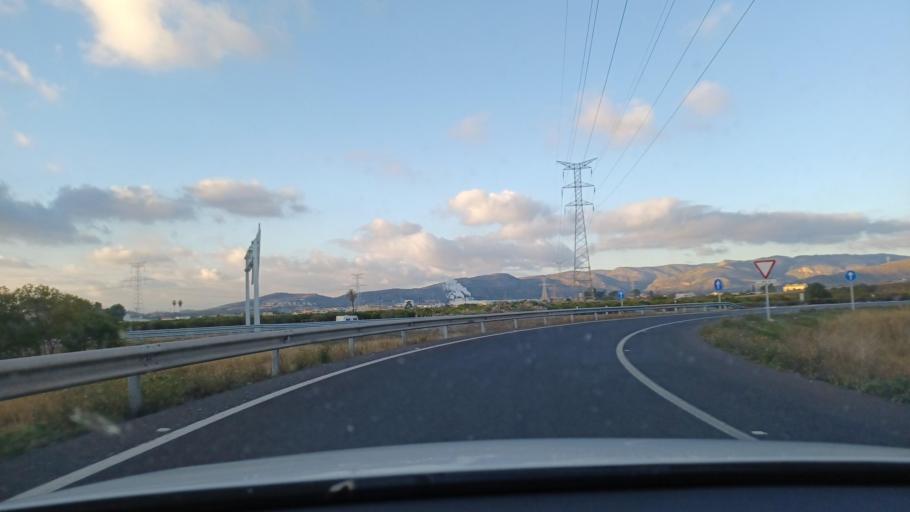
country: ES
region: Valencia
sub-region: Provincia de Castello
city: Vila-real
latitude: 39.9841
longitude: -0.0945
